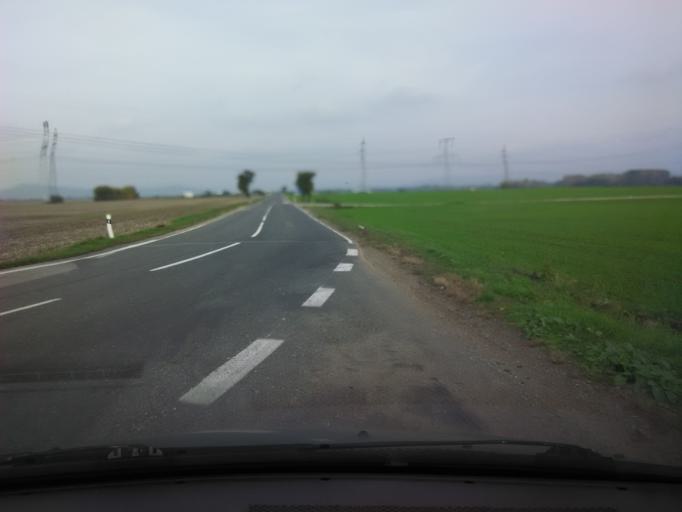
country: SK
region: Nitriansky
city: Tlmace
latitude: 48.2138
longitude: 18.5194
